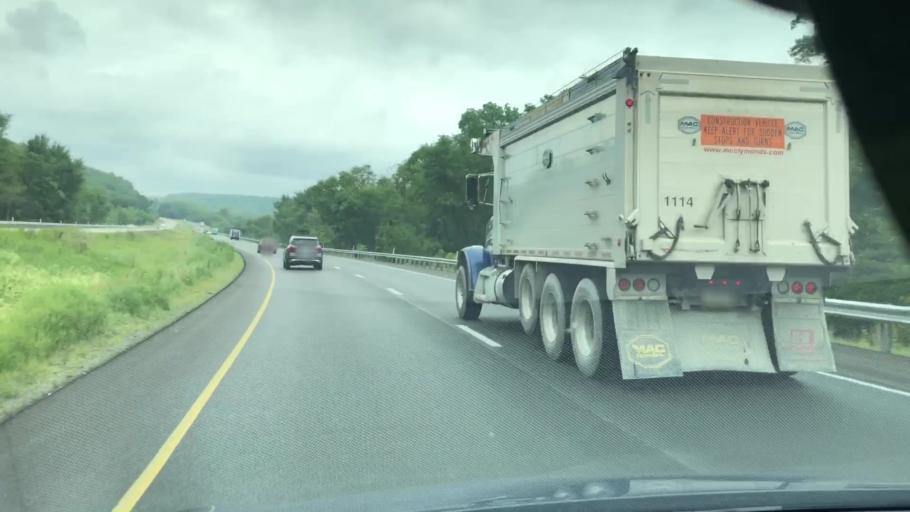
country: US
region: Pennsylvania
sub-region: Butler County
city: Zelienople
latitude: 40.8416
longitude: -80.1023
